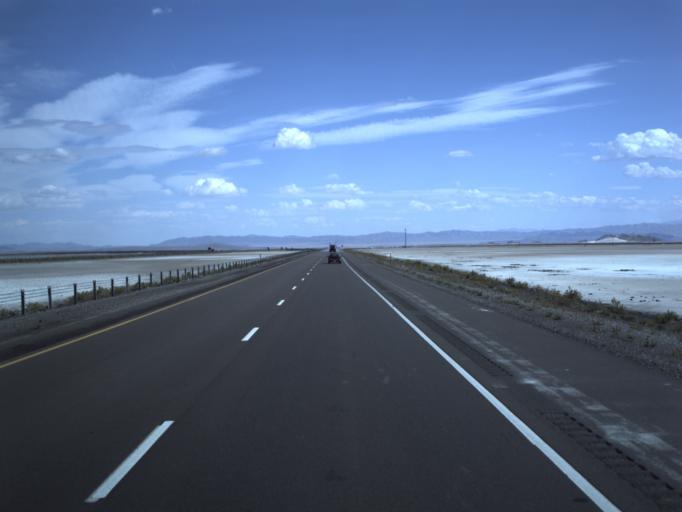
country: US
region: Utah
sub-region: Tooele County
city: Wendover
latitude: 40.7281
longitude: -113.3783
